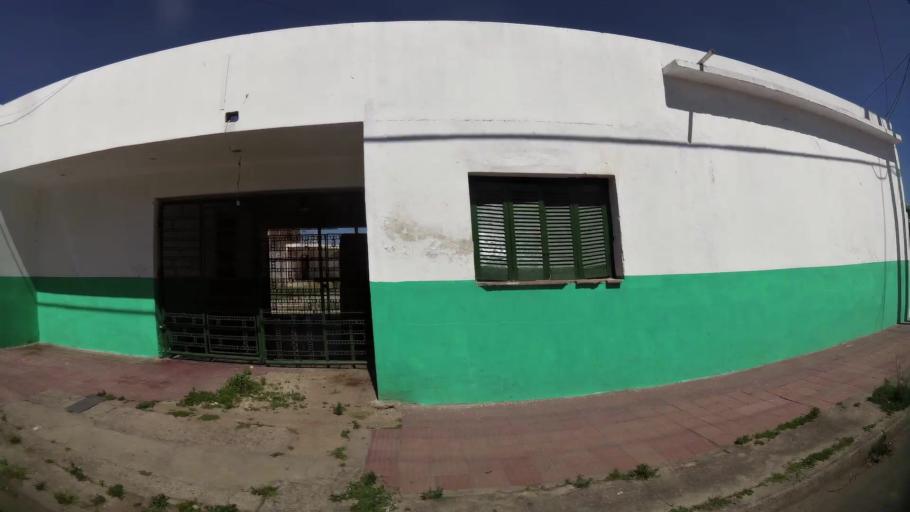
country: AR
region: Cordoba
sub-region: Departamento de Capital
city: Cordoba
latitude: -31.4394
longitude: -64.1357
